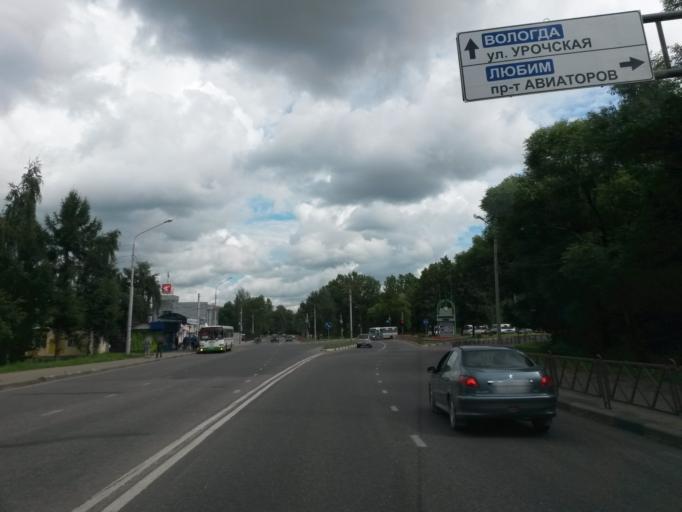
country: RU
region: Jaroslavl
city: Yaroslavl
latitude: 57.6442
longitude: 39.9053
